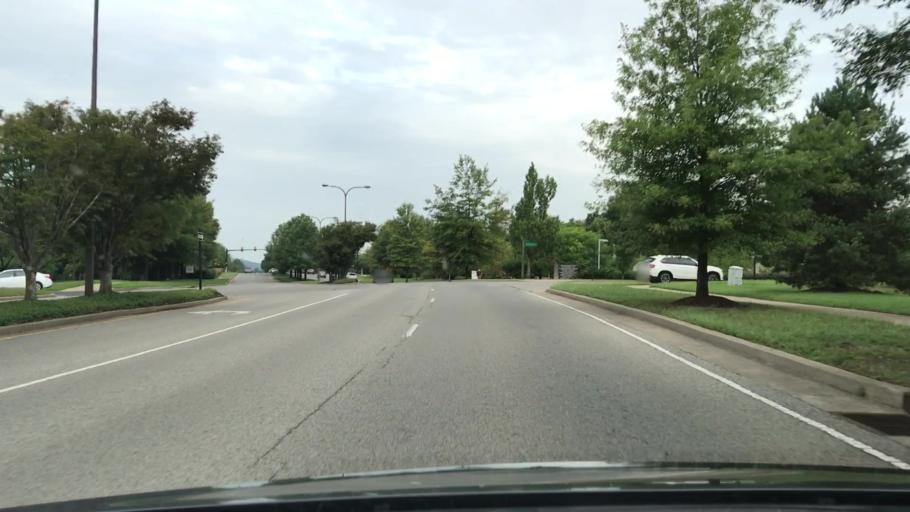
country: US
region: Tennessee
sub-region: Williamson County
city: Franklin
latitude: 35.9447
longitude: -86.8022
